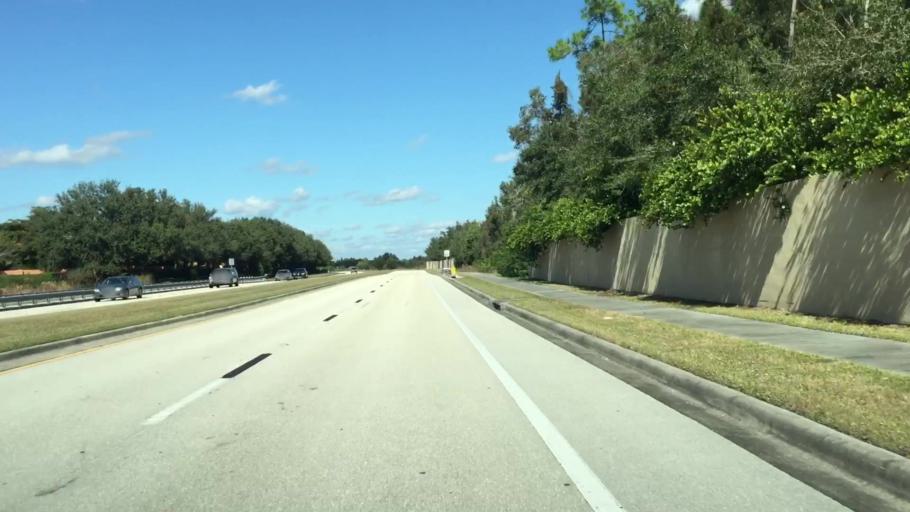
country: US
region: Florida
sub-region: Lee County
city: Estero
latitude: 26.4123
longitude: -81.8047
